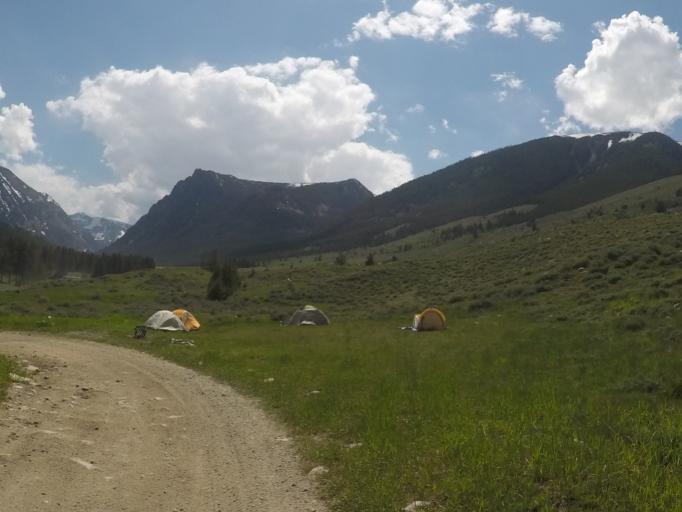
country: US
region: Montana
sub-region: Carbon County
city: Red Lodge
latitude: 45.0602
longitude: -109.4119
